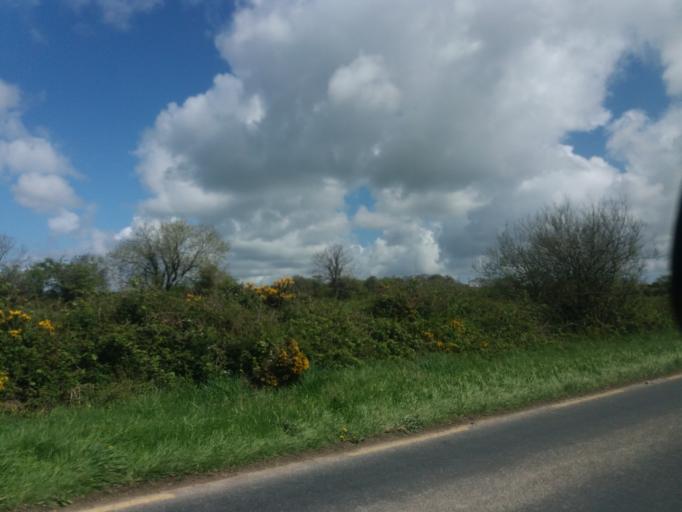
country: IE
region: Leinster
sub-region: Loch Garman
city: Loch Garman
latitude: 52.2839
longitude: -6.6407
